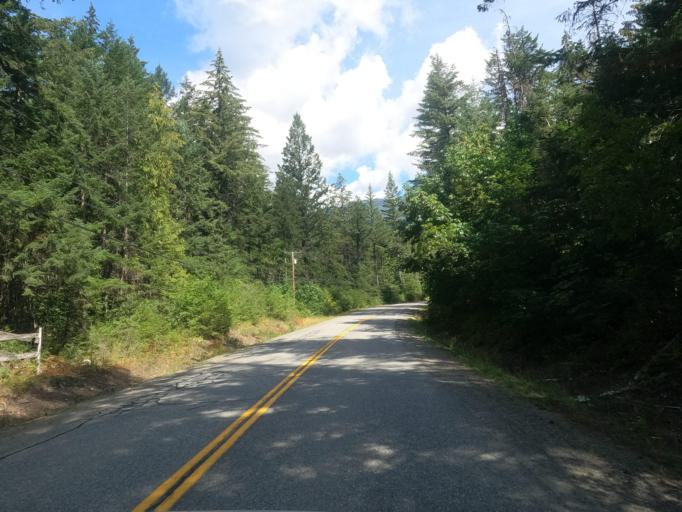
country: CA
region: British Columbia
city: Pemberton
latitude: 50.3492
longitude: -122.7349
